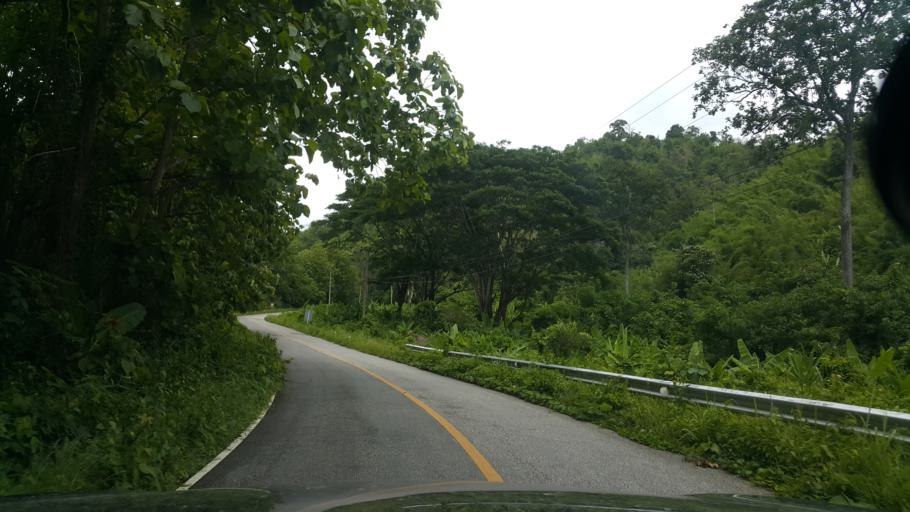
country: TH
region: Loei
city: Na Haeo
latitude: 17.6374
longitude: 100.9029
